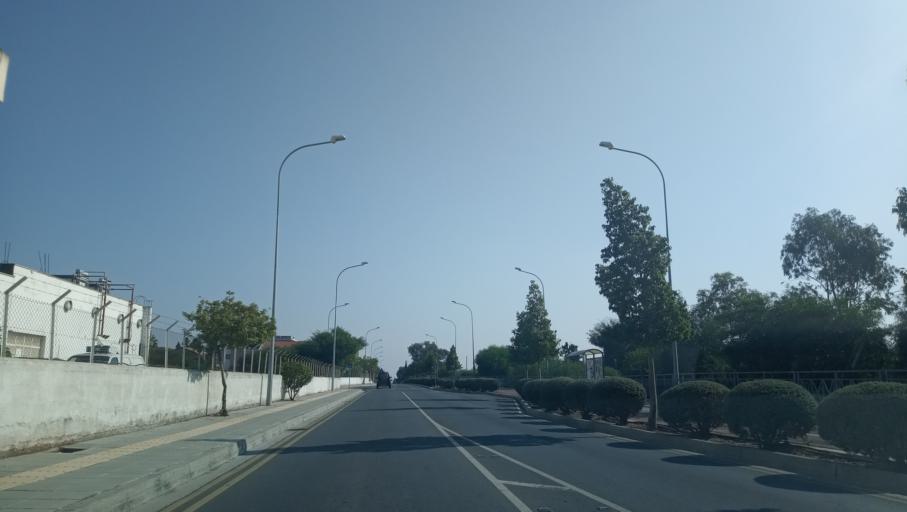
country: CY
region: Lefkosia
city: Nicosia
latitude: 35.1449
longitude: 33.3825
